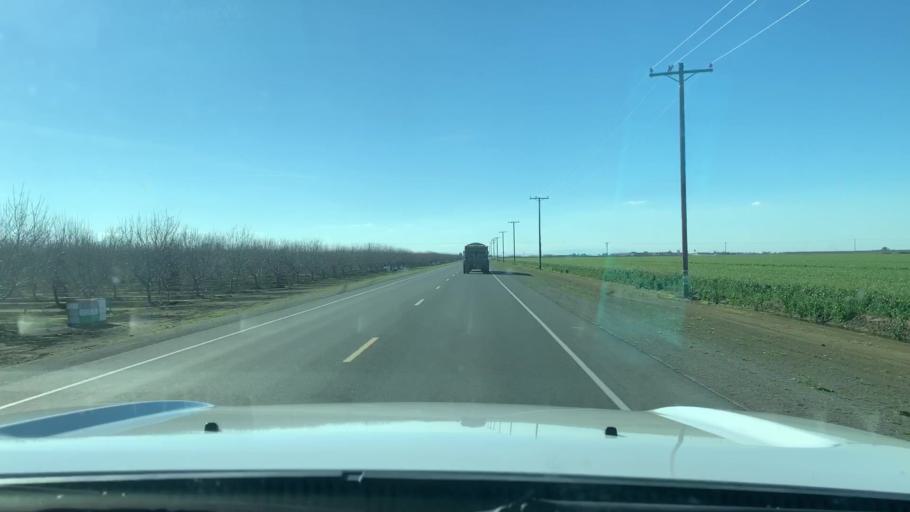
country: US
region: California
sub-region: Kings County
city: Corcoran
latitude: 36.2109
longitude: -119.5046
